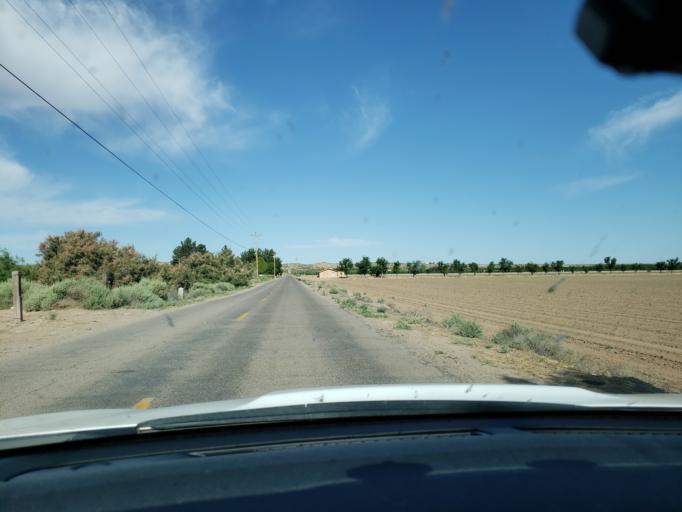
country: US
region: New Mexico
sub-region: Dona Ana County
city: Vado
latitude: 32.0826
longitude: -106.6940
